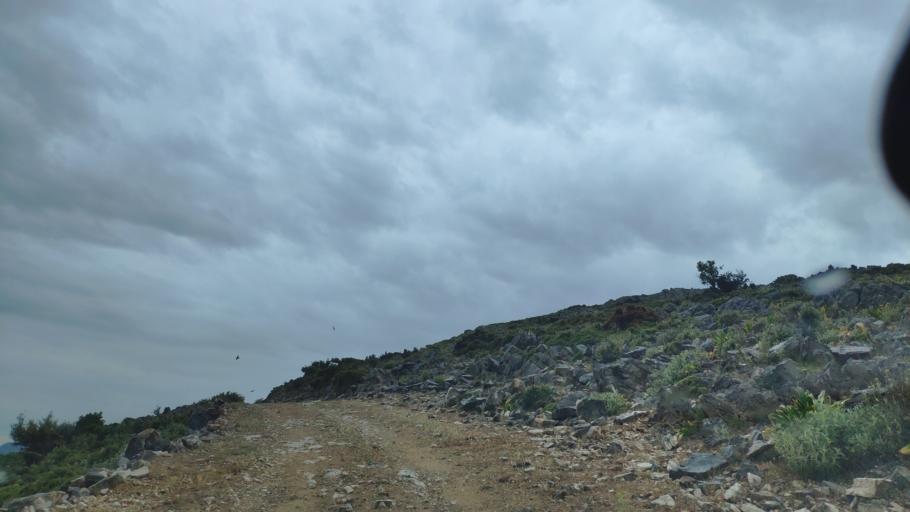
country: GR
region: West Greece
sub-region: Nomos Aitolias kai Akarnanias
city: Archontochorion
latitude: 38.6759
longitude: 21.0147
